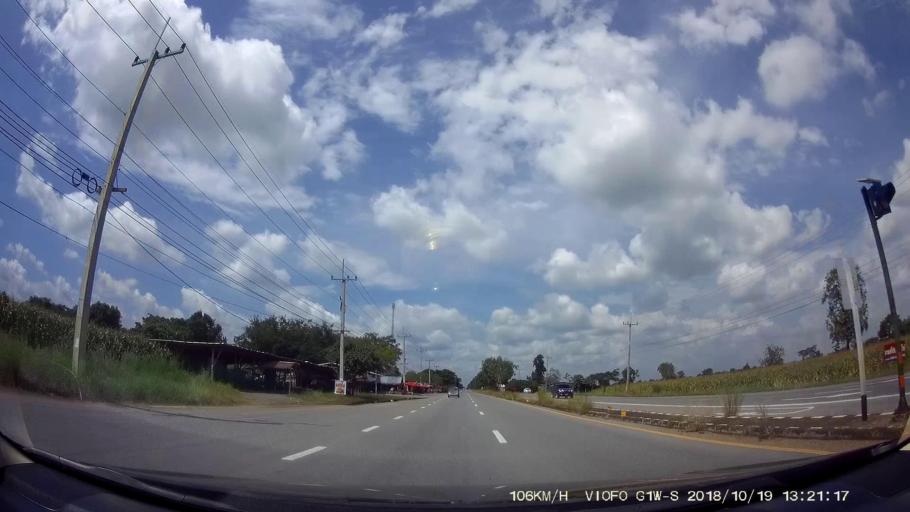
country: TH
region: Chaiyaphum
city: Chatturat
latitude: 15.4593
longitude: 101.8264
